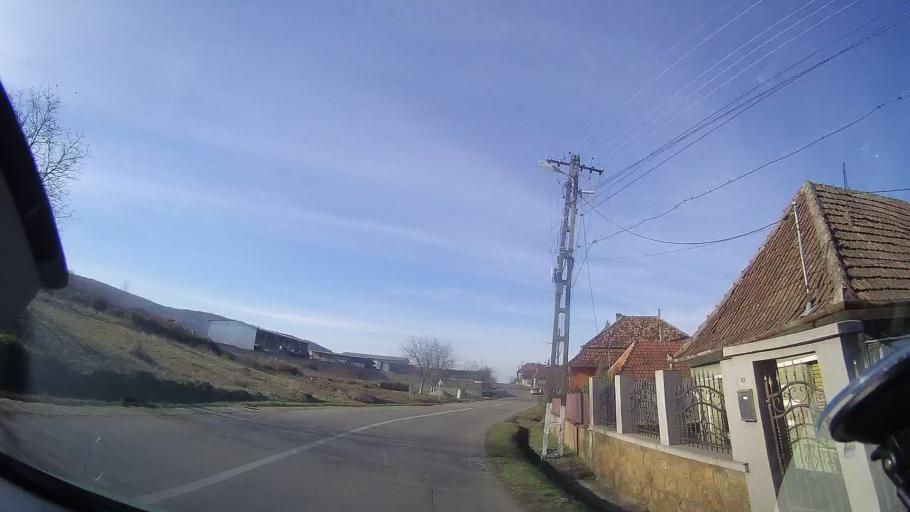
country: RO
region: Bihor
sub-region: Comuna Magesti
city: Magesti
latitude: 47.0186
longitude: 22.4271
